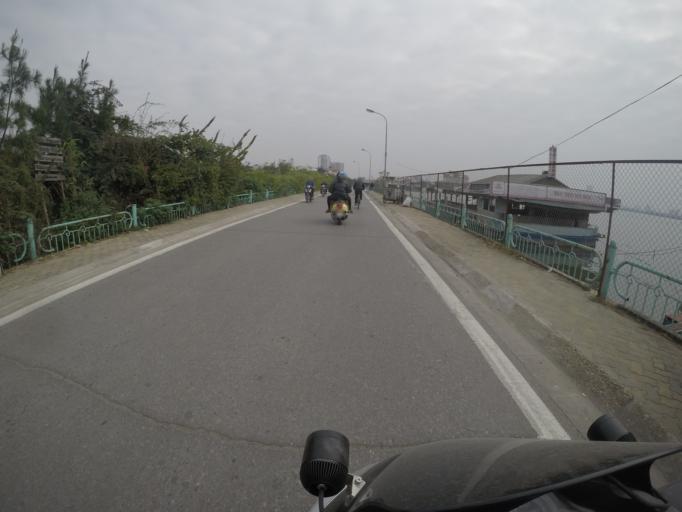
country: VN
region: Ha Noi
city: Tay Ho
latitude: 21.0736
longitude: 105.8201
